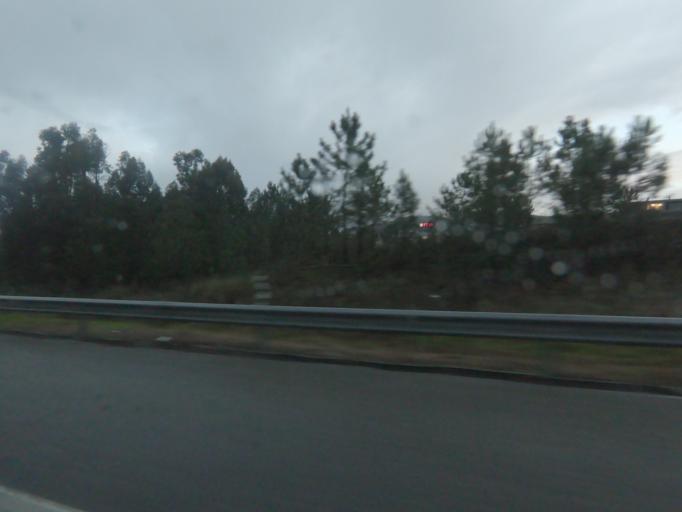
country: PT
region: Braga
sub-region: Braga
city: Oliveira
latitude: 41.5314
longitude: -8.4859
